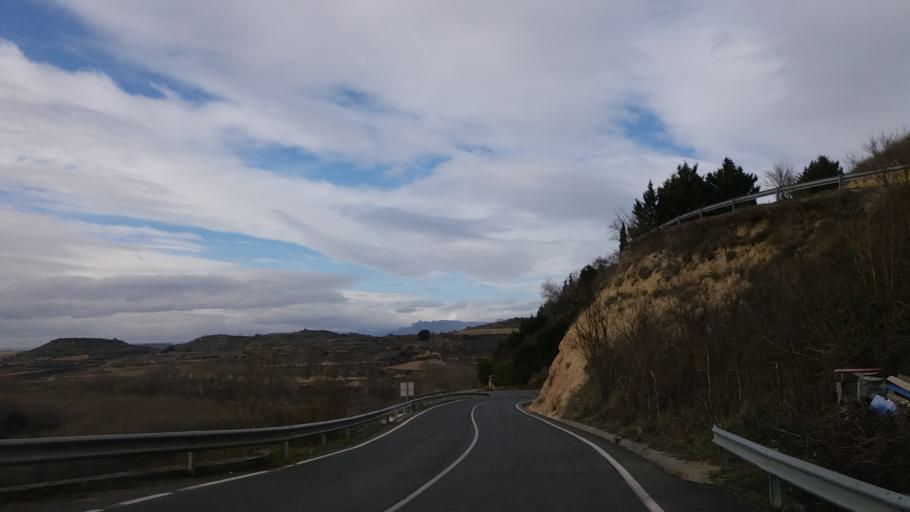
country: ES
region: La Rioja
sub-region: Provincia de La Rioja
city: San Vicente de la Sonsierra
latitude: 42.5635
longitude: -2.7617
